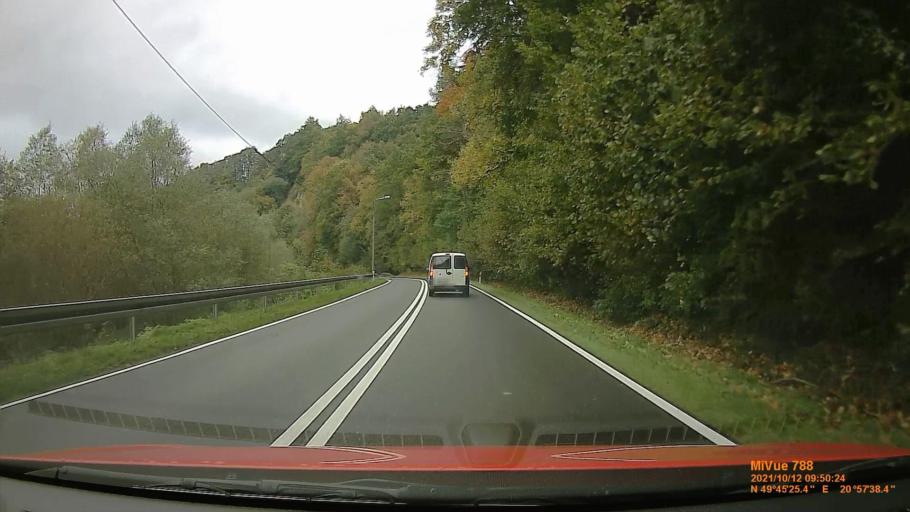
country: PL
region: Lesser Poland Voivodeship
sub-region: Powiat tarnowski
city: Ciezkowice
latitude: 49.7571
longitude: 20.9608
